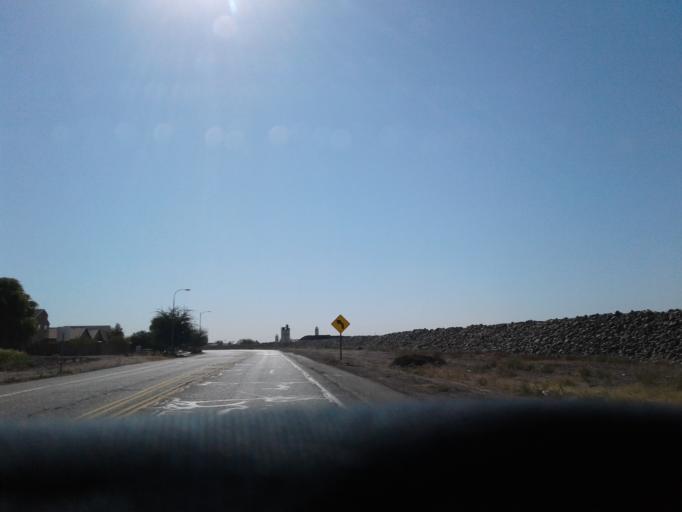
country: US
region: Arizona
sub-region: Maricopa County
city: Laveen
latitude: 33.4079
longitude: -112.1832
